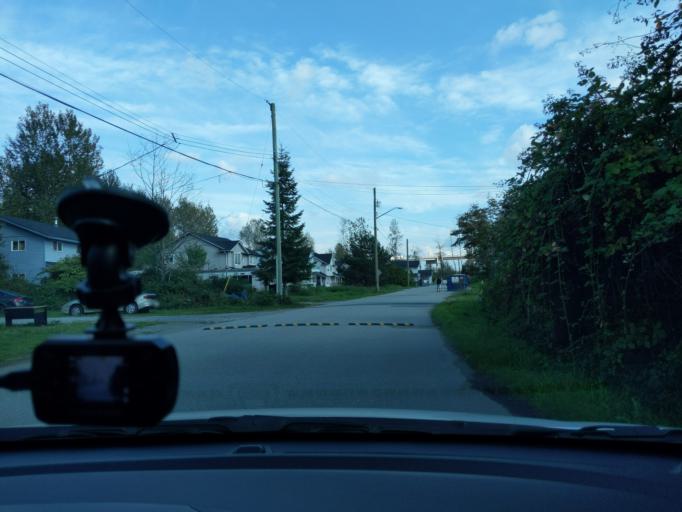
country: CA
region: British Columbia
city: Pitt Meadows
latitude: 49.2019
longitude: -122.6758
